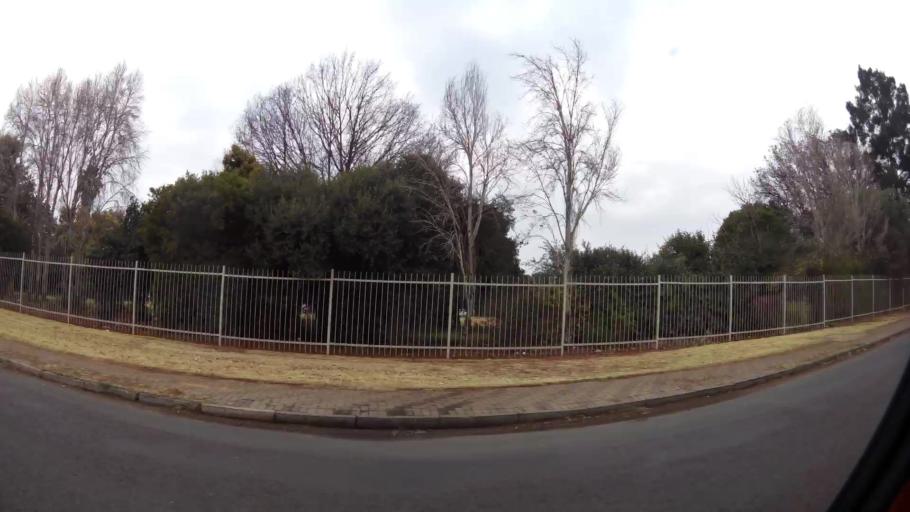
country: ZA
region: Gauteng
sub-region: Sedibeng District Municipality
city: Vanderbijlpark
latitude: -26.7031
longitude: 27.8364
